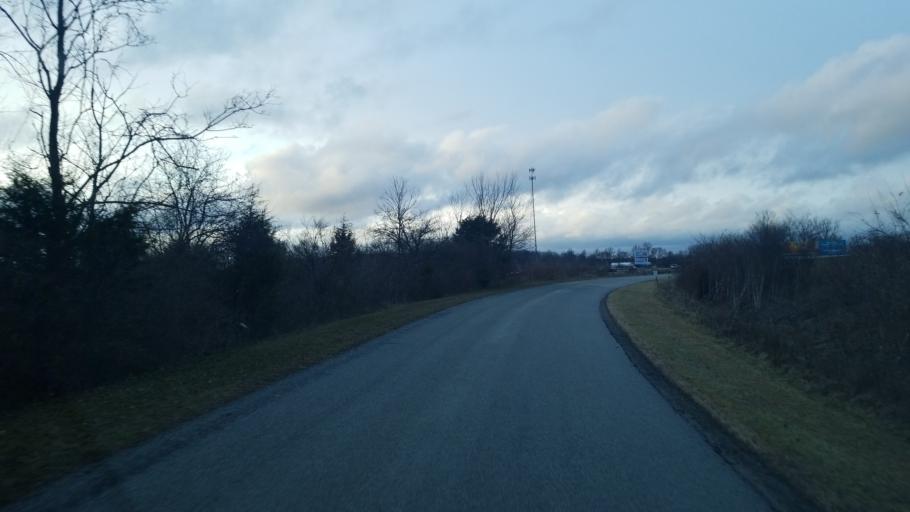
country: US
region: Ohio
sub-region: Marion County
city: Prospect
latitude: 40.4353
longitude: -83.0715
